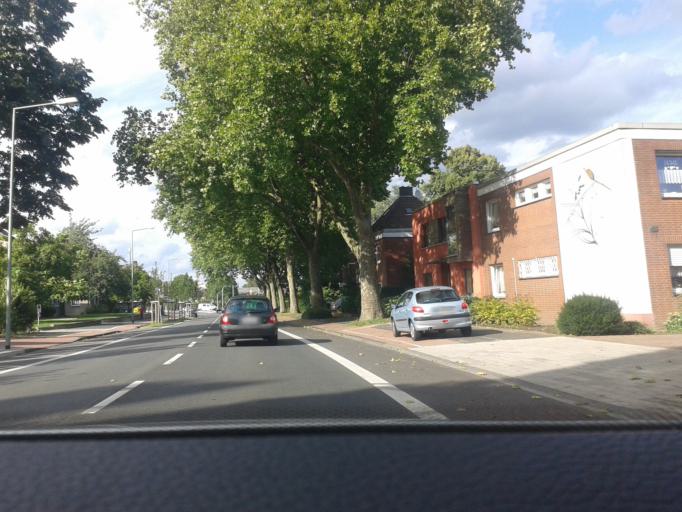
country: DE
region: North Rhine-Westphalia
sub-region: Regierungsbezirk Dusseldorf
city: Hochfeld
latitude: 51.4220
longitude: 6.6987
